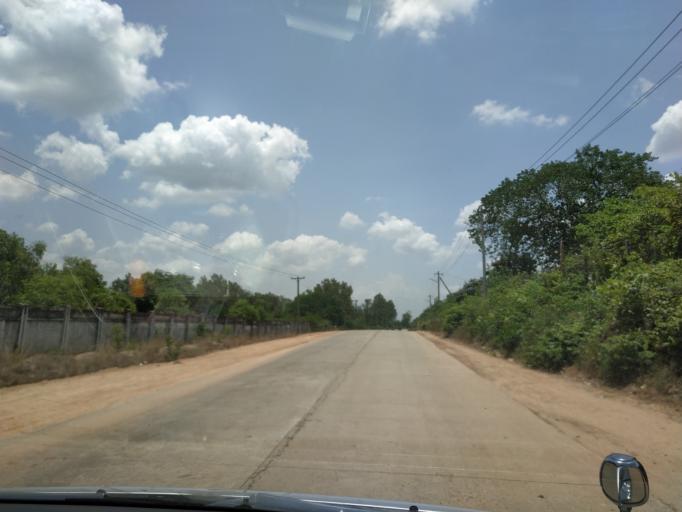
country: MM
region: Bago
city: Bago
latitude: 17.4705
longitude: 96.4694
